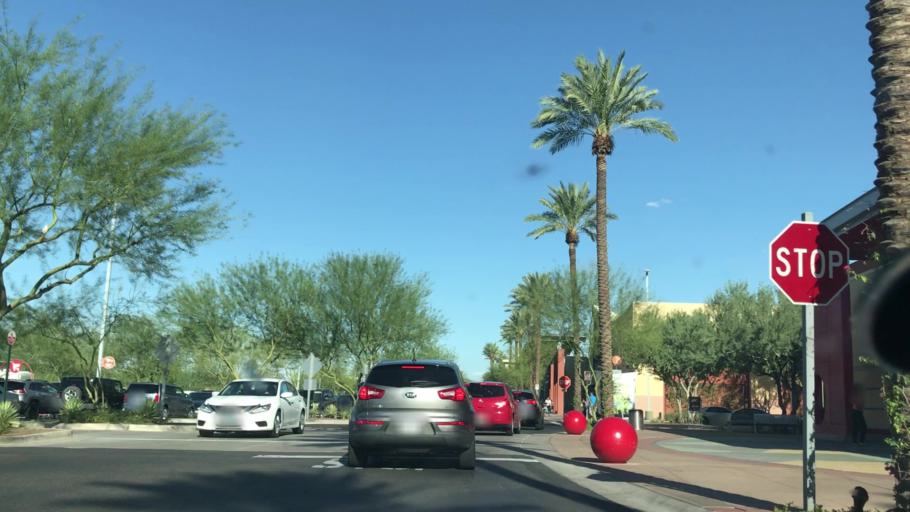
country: US
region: Arizona
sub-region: Maricopa County
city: Tempe
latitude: 33.4304
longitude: -111.9055
